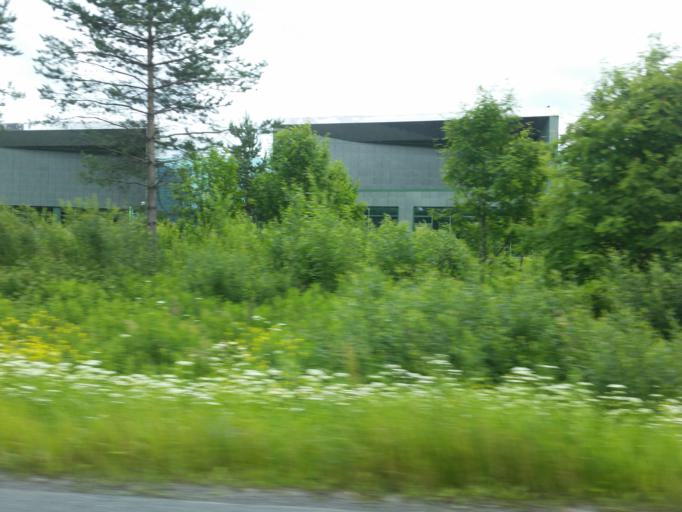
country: FI
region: Northern Savo
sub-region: Kuopio
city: Kuopio
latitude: 62.8863
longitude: 27.6290
